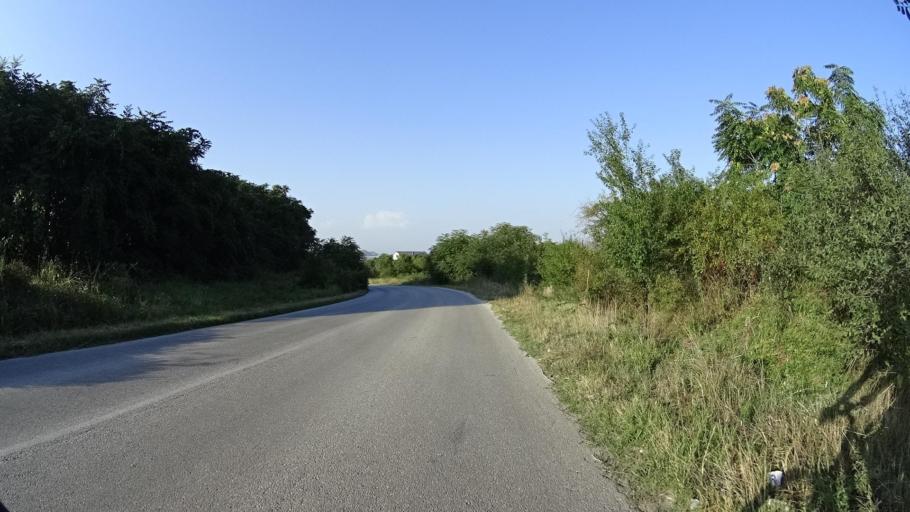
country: BG
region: Plovdiv
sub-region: Obshtina Plovdiv
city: Plovdiv
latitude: 42.0765
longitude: 24.7018
